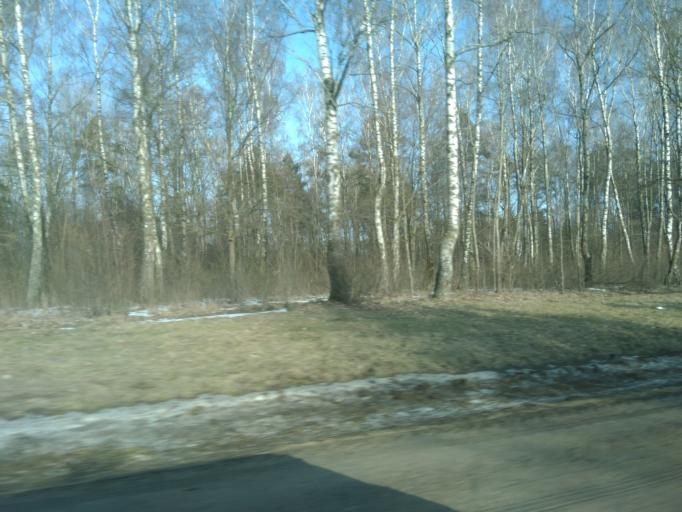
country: BY
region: Minsk
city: Snow
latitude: 53.2163
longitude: 26.4383
